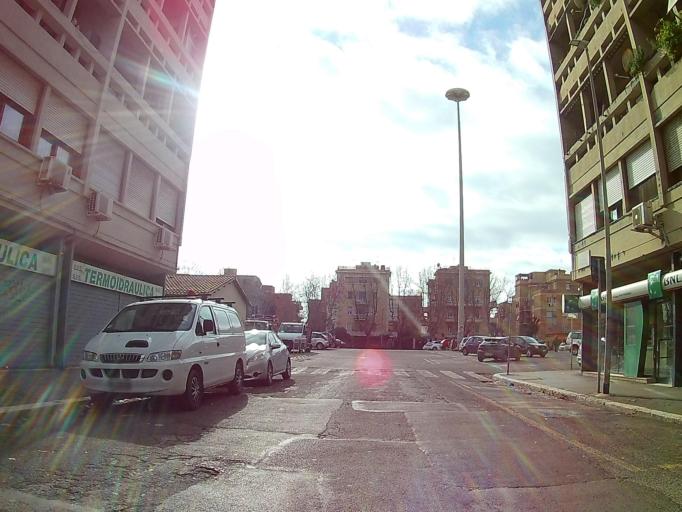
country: IT
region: Latium
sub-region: Citta metropolitana di Roma Capitale
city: Lido di Ostia
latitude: 41.7324
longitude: 12.2749
